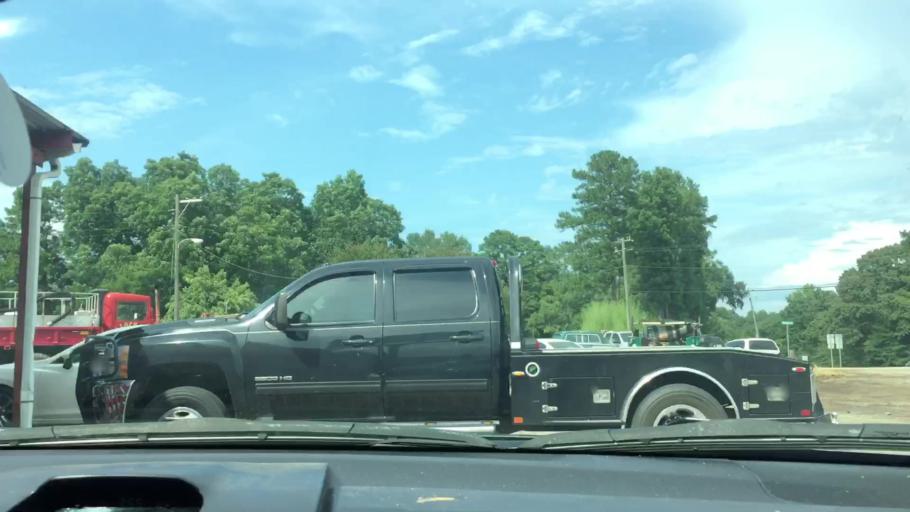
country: US
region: Alabama
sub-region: Hale County
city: Greensboro
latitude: 32.6919
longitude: -87.6085
